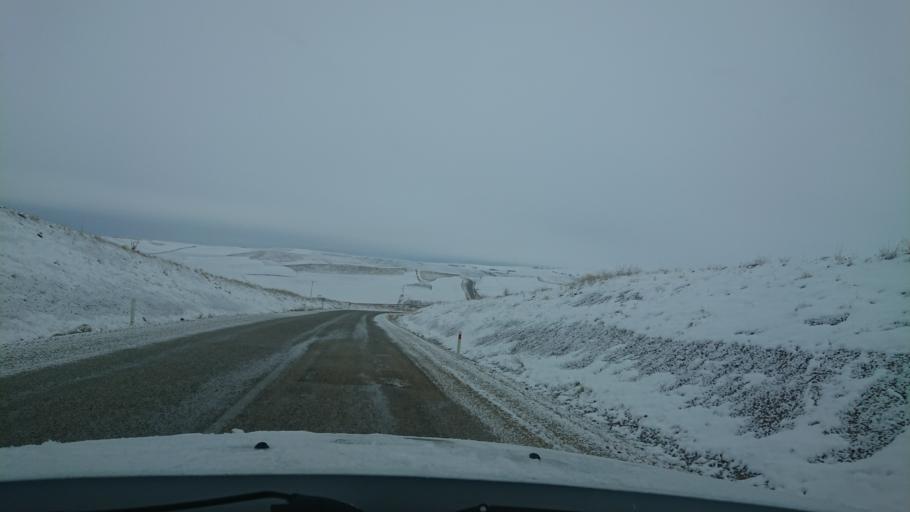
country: TR
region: Aksaray
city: Agacoren
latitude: 38.7825
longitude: 33.8713
